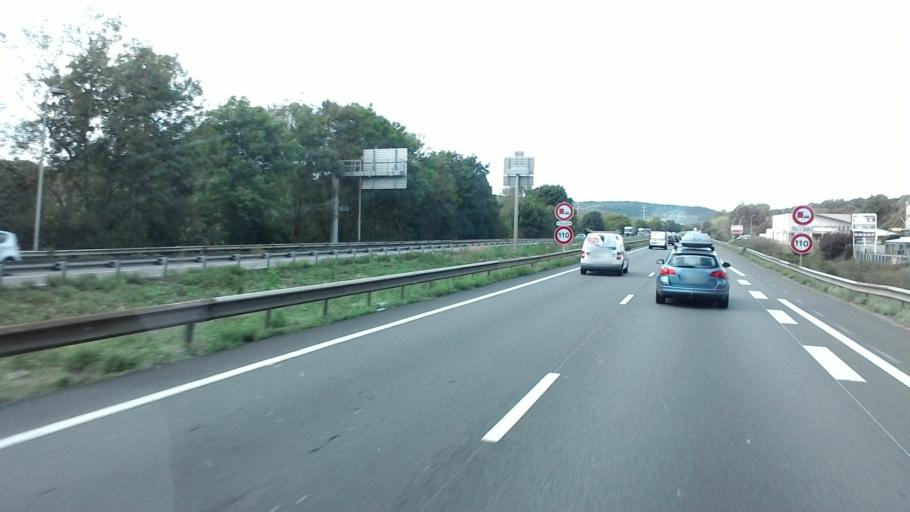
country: FR
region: Lorraine
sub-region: Departement de Meurthe-et-Moselle
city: Bouxieres-aux-Dames
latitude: 48.7566
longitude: 6.1535
